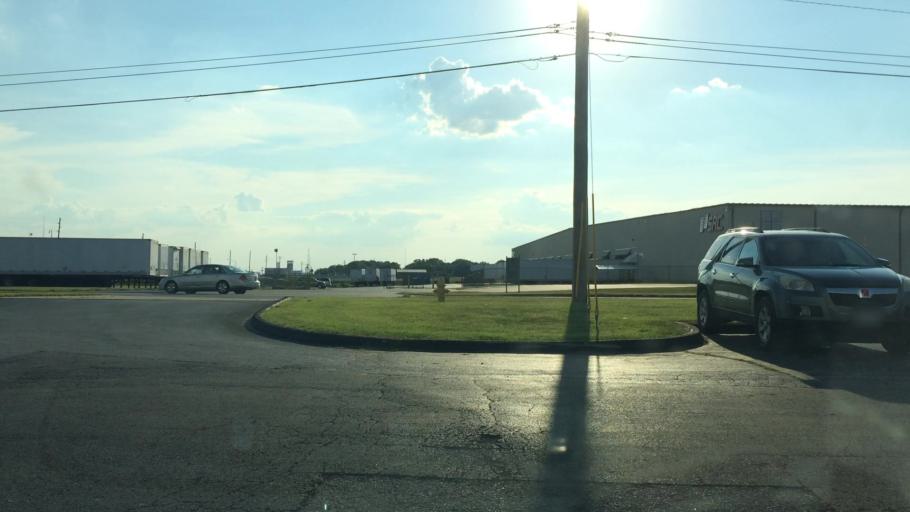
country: US
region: Missouri
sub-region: Greene County
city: Springfield
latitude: 37.2152
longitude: -93.2545
